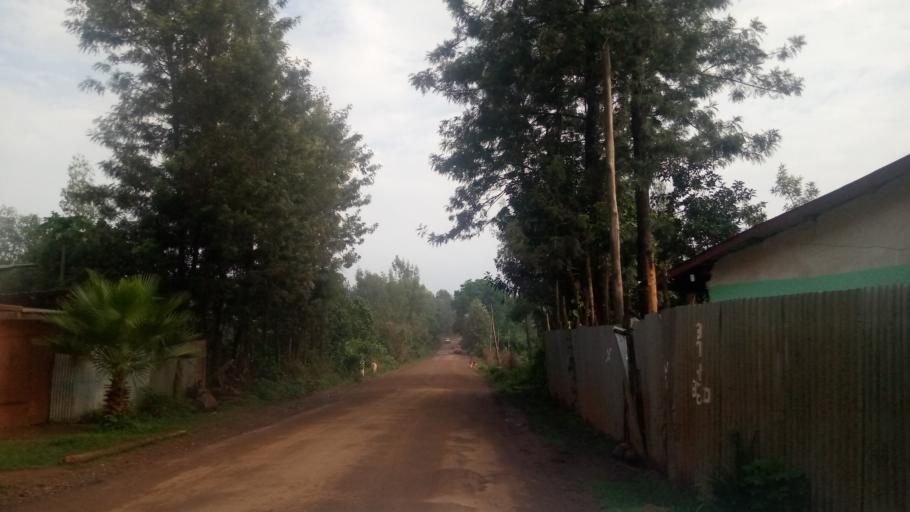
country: ET
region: Oromiya
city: Agaro
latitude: 7.8416
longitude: 36.6617
